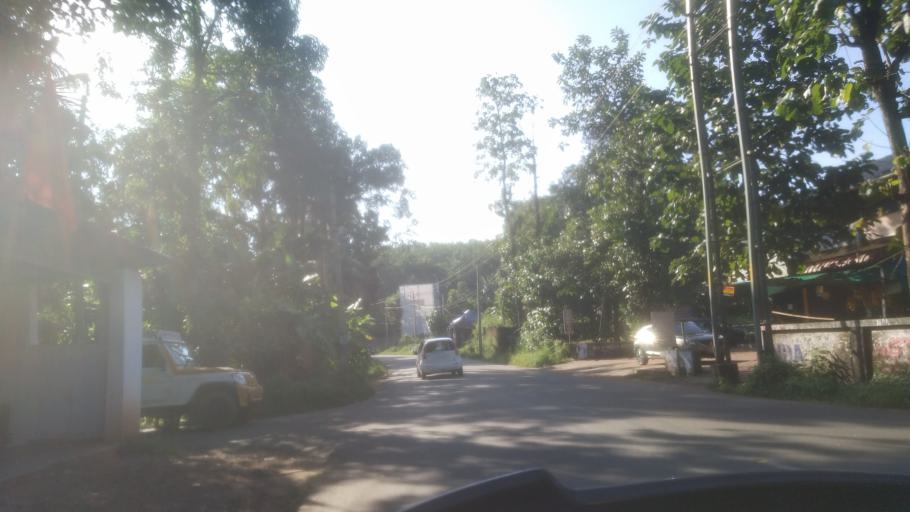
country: IN
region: Kerala
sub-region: Ernakulam
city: Ramamangalam
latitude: 9.9781
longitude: 76.4933
